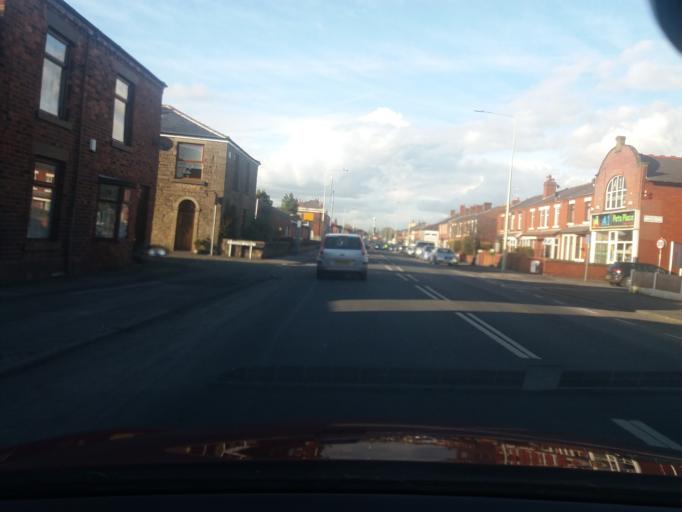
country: GB
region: England
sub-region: Lancashire
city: Chorley
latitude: 53.6576
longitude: -2.6192
